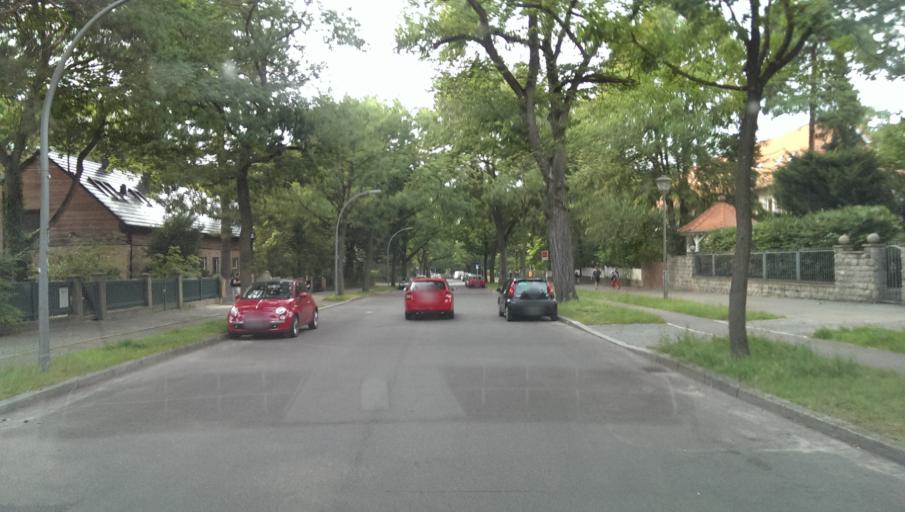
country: DE
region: Berlin
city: Zehlendorf Bezirk
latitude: 52.4455
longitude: 13.2339
